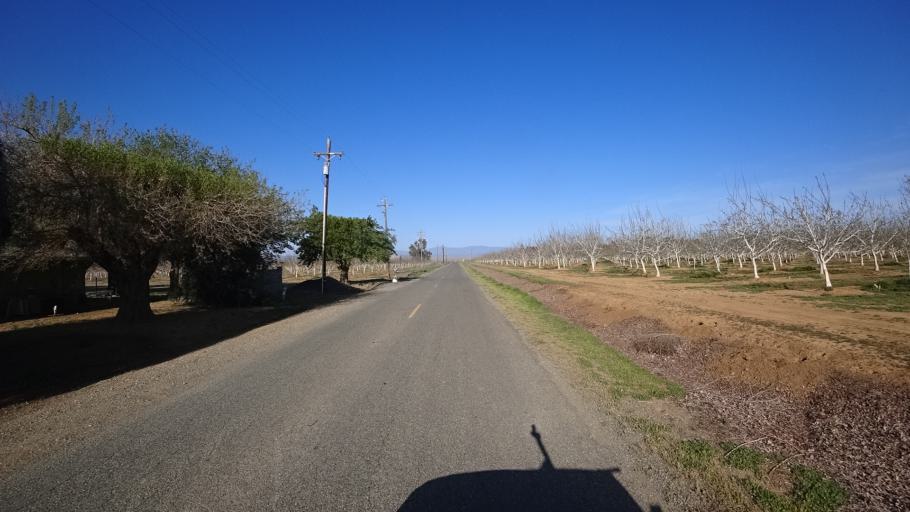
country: US
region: California
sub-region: Glenn County
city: Willows
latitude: 39.5095
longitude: -122.2443
